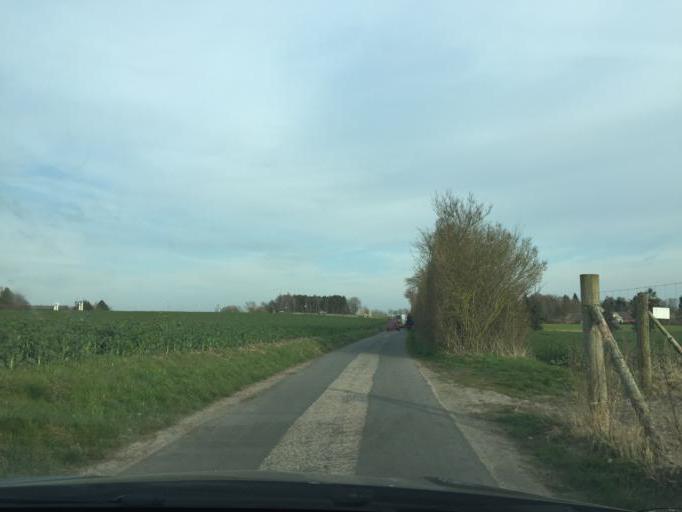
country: DK
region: South Denmark
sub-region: Kerteminde Kommune
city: Langeskov
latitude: 55.3184
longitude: 10.5706
